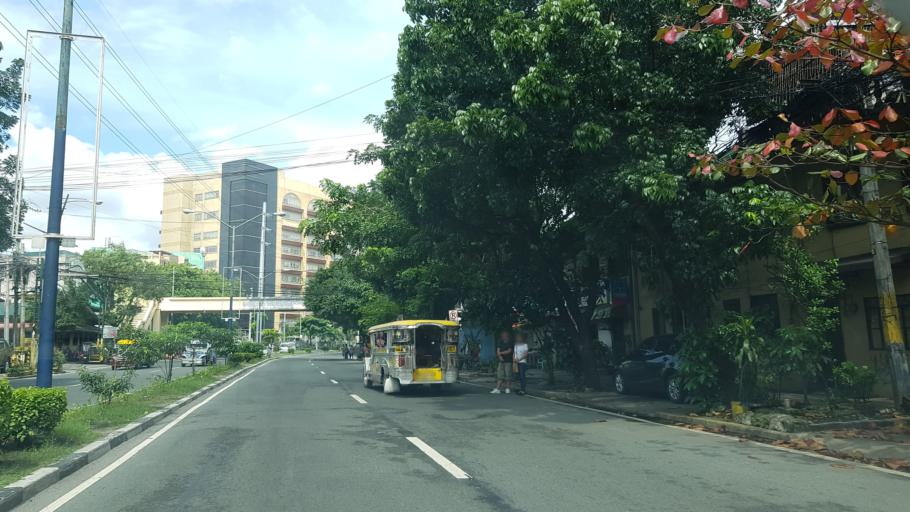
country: PH
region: Metro Manila
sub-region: Makati City
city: Makati City
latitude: 14.5620
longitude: 121.0507
